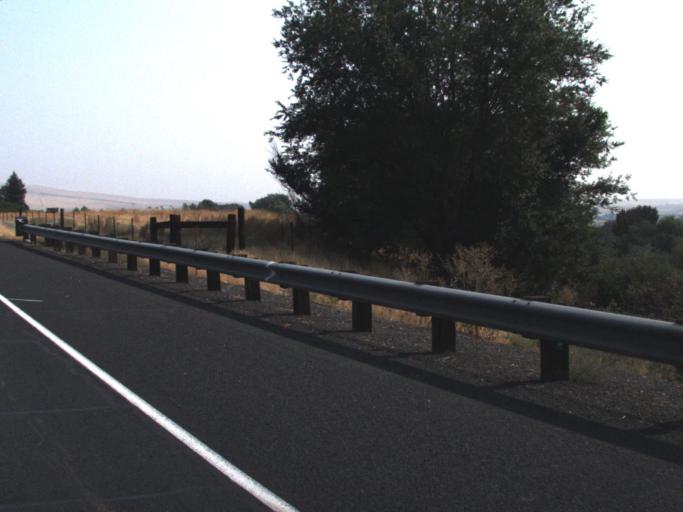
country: US
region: Washington
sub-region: Yakima County
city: Selah
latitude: 46.6774
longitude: -120.5082
